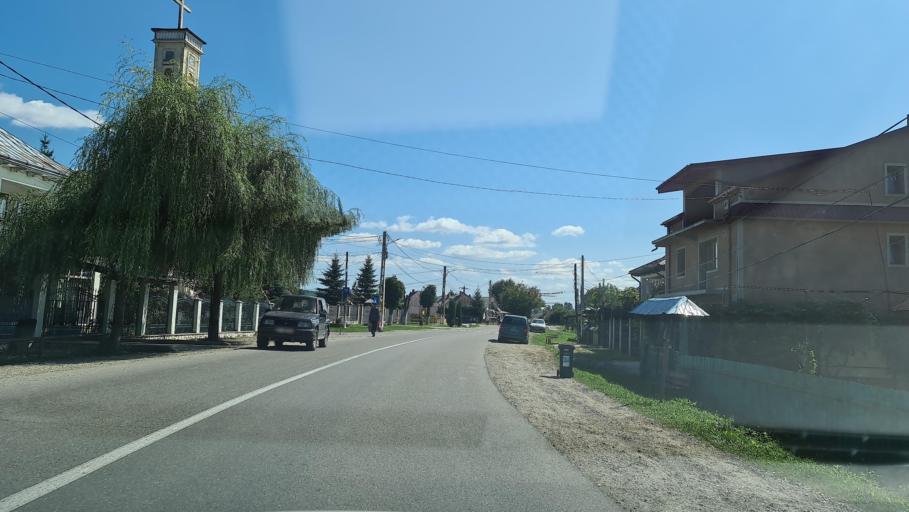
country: RO
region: Bacau
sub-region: Comuna Balcani
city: Frumoasa
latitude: 46.6635
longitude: 26.5395
